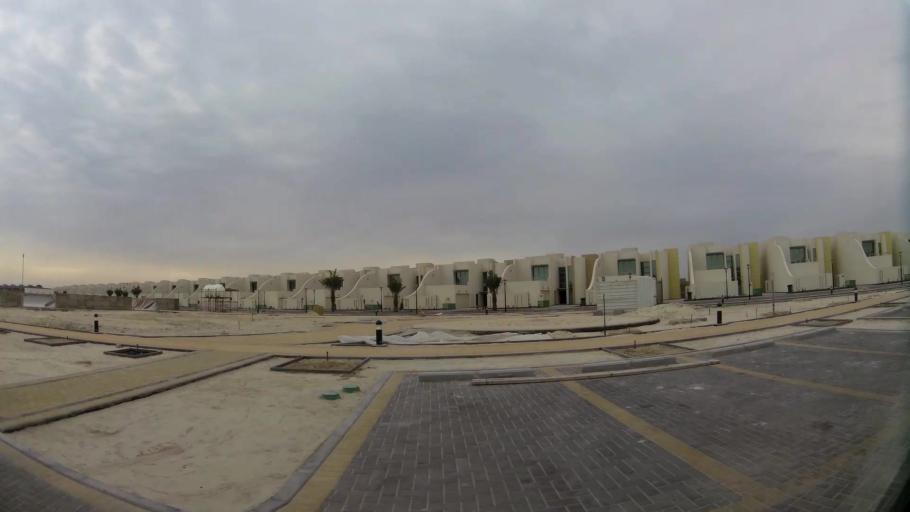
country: BH
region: Central Governorate
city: Dar Kulayb
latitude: 25.8297
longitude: 50.6047
